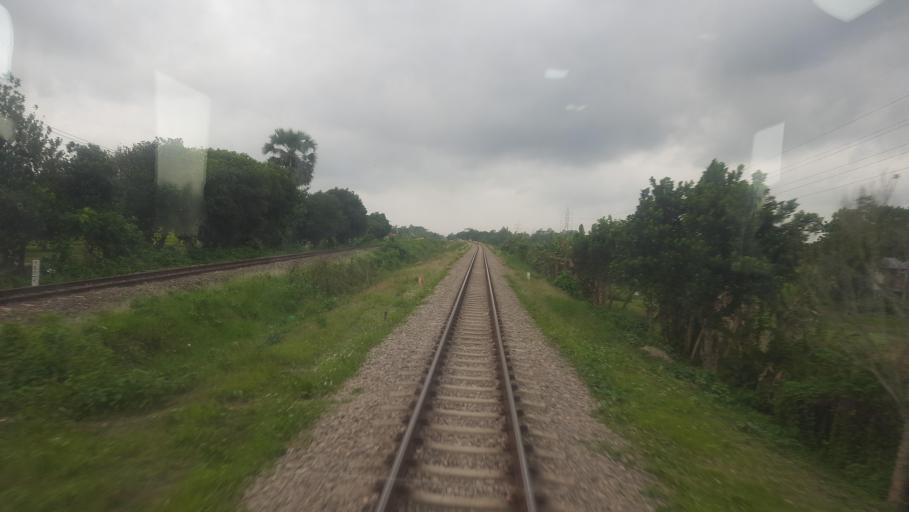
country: BD
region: Dhaka
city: Narsingdi
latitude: 23.9813
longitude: 90.8443
